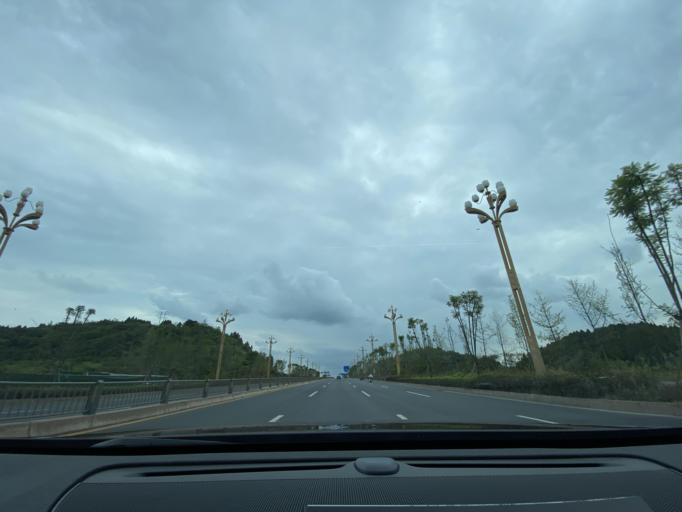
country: CN
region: Sichuan
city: Jiancheng
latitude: 30.4521
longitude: 104.4959
